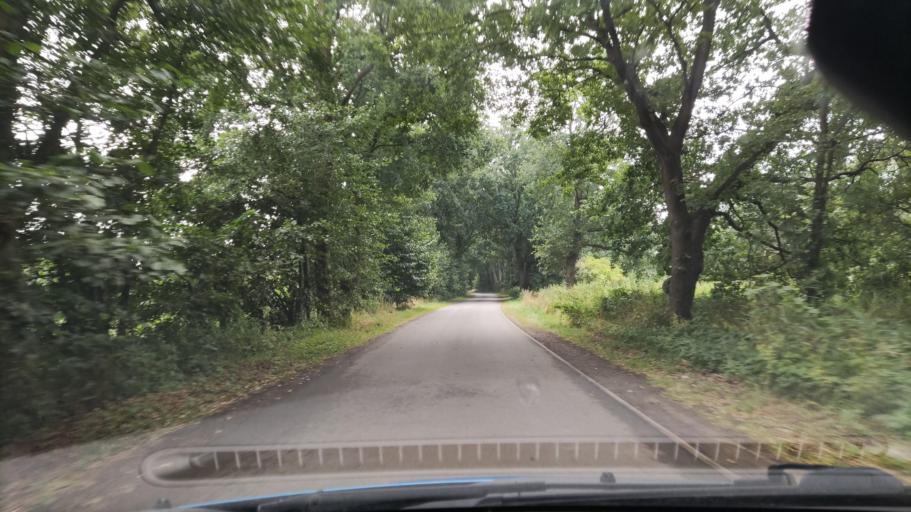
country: DE
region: Lower Saxony
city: Wittorf
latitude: 53.3499
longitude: 10.3731
